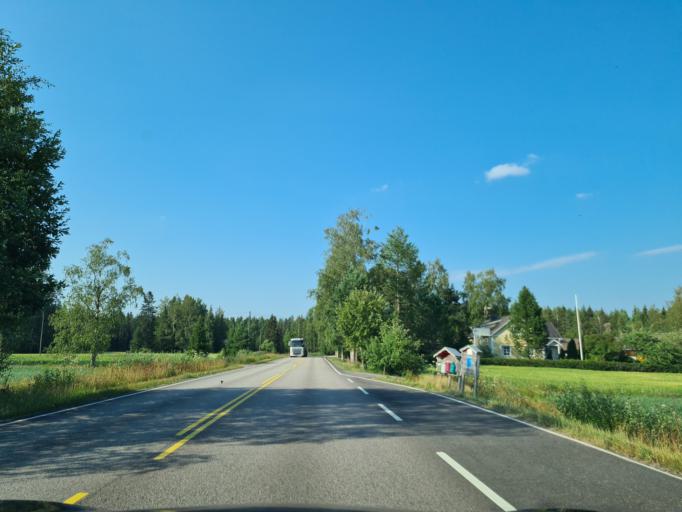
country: FI
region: Satakunta
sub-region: Pohjois-Satakunta
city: Karvia
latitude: 62.1996
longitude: 22.5967
